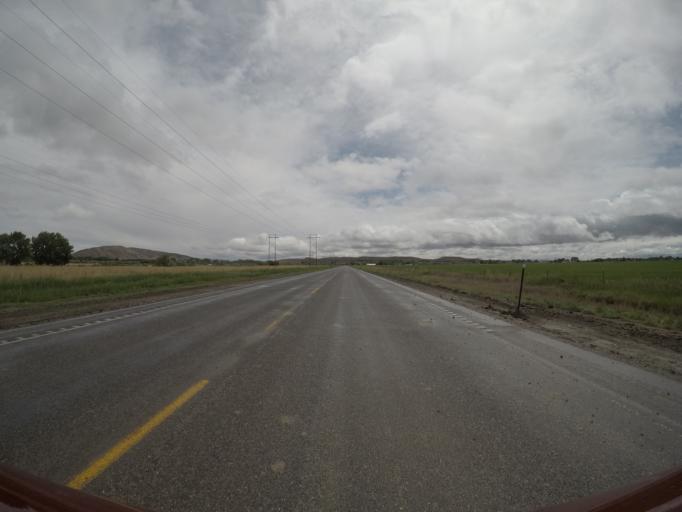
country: US
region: Wyoming
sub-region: Big Horn County
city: Lovell
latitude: 44.8494
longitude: -108.3316
